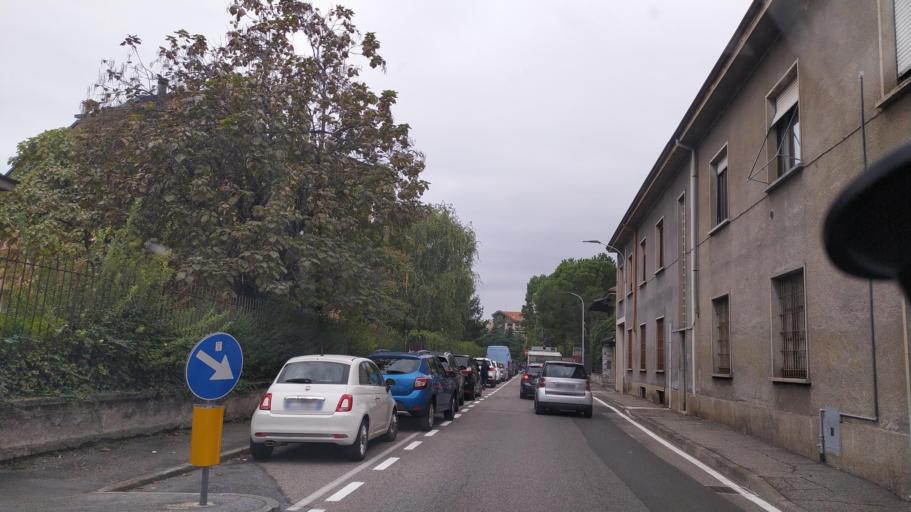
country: IT
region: Lombardy
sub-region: Provincia di Monza e Brianza
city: Seregno
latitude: 45.6449
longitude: 9.2111
